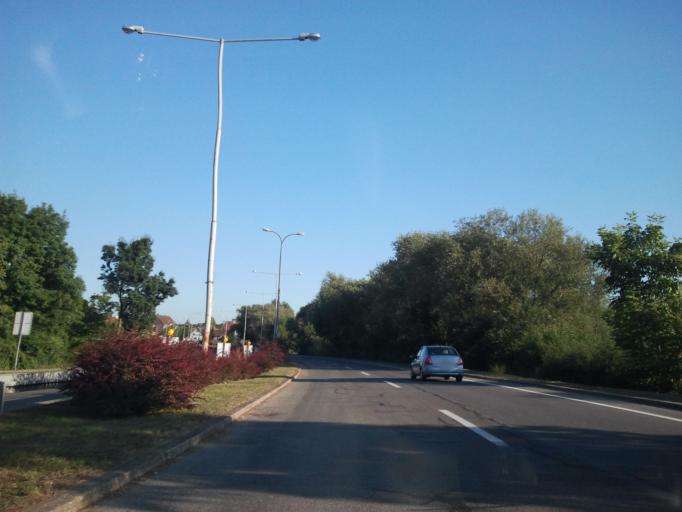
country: HR
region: Sisacko-Moslavacka
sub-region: Grad Sisak
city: Sisak
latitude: 45.4851
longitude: 16.3645
